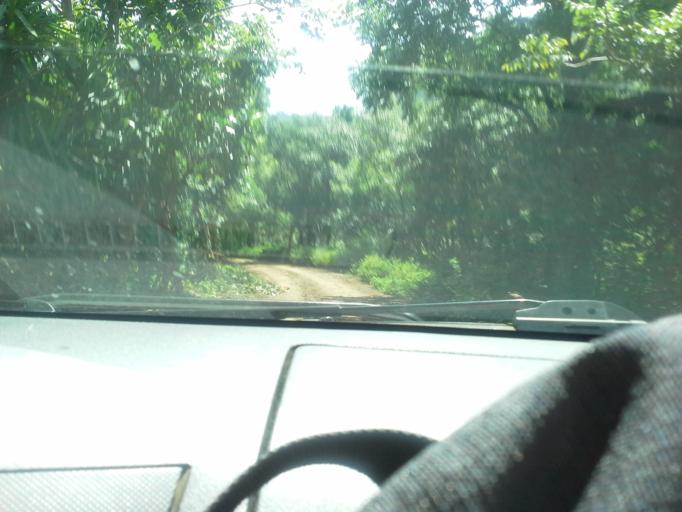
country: NI
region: Matagalpa
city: Terrabona
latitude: 12.7362
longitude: -85.9268
